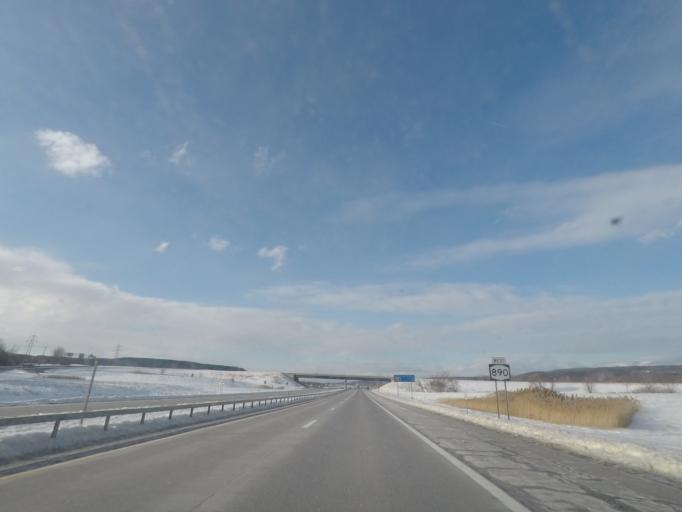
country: US
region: New York
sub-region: Schenectady County
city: Scotia
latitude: 42.8397
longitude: -74.0022
